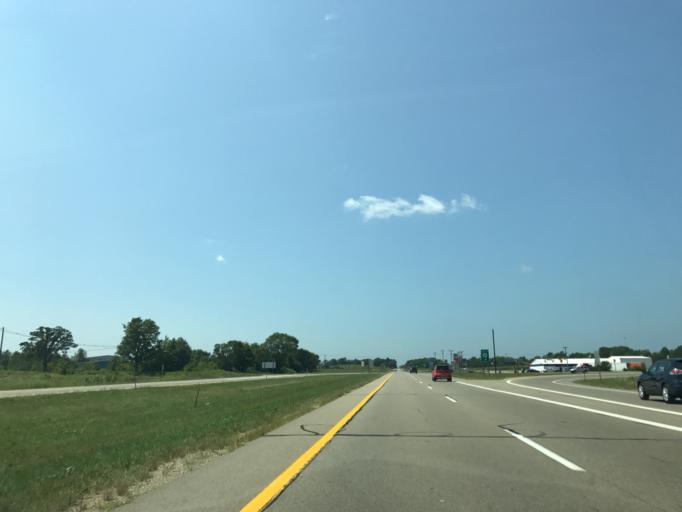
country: US
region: Michigan
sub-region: Berrien County
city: Buchanan
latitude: 41.8052
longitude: -86.3171
